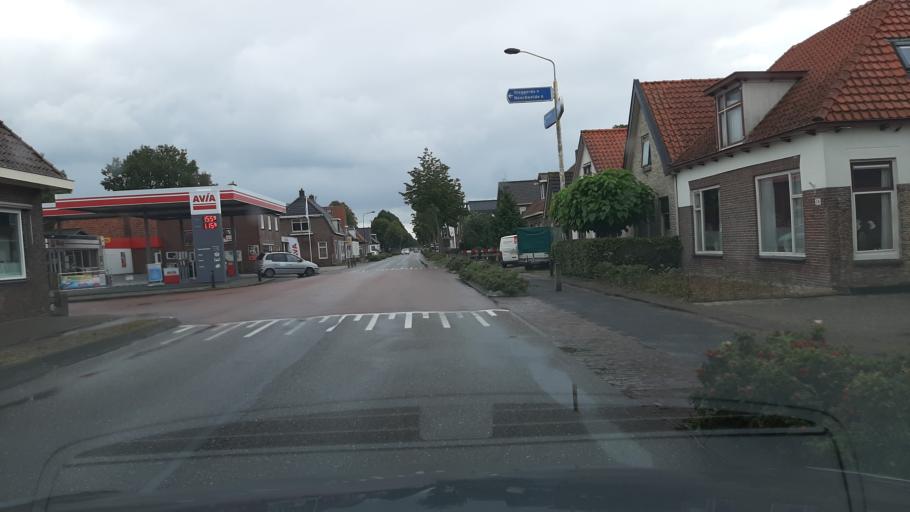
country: NL
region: Friesland
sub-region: Gemeente Weststellingwerf
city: Steggerda
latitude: 52.8445
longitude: 6.0386
